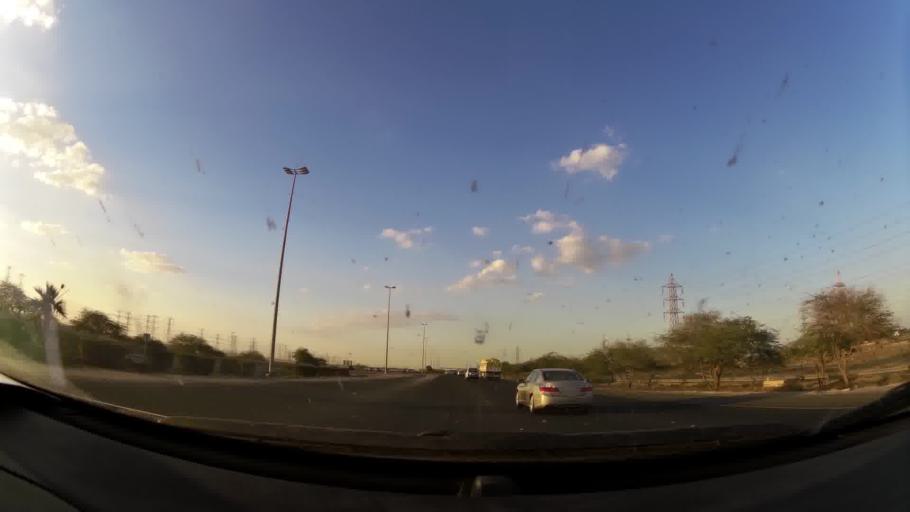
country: KW
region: Al Ahmadi
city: Al Fahahil
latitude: 28.8999
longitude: 48.2194
